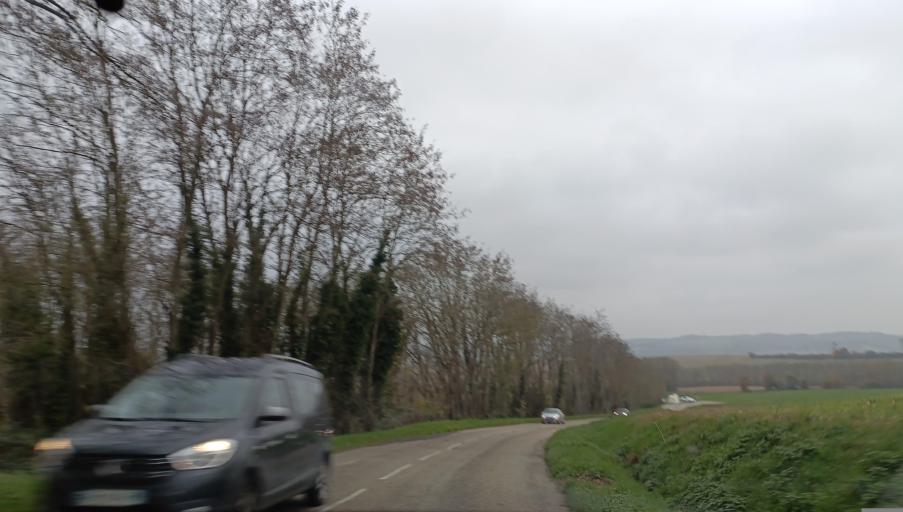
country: FR
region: Rhone-Alpes
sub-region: Departement de l'Isere
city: Serpaize
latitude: 45.5645
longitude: 4.9115
